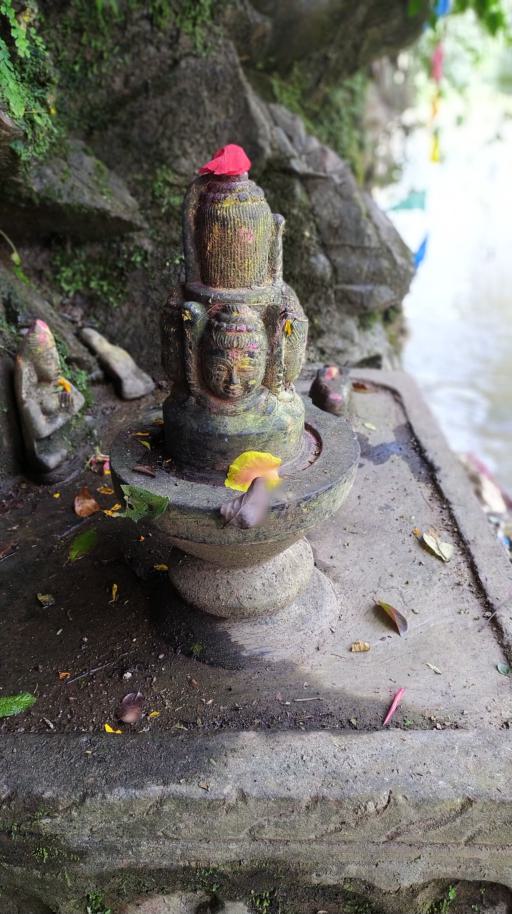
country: NP
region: Central Region
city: Panaoti
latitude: 27.5697
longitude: 85.5391
